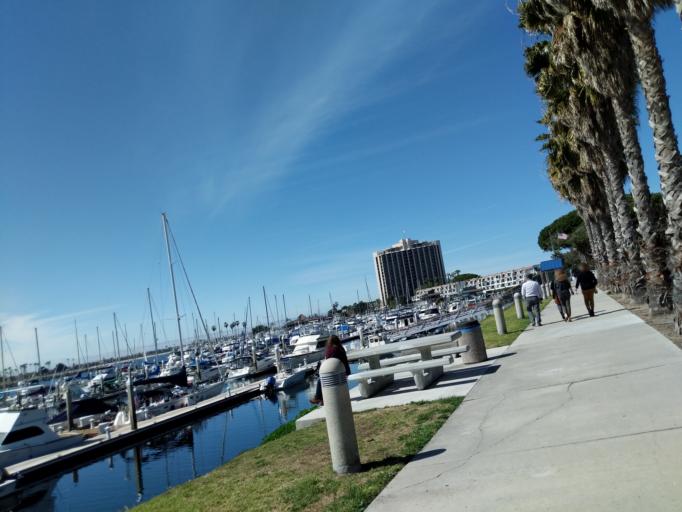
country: US
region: California
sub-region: San Diego County
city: San Diego
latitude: 32.7632
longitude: -117.2360
